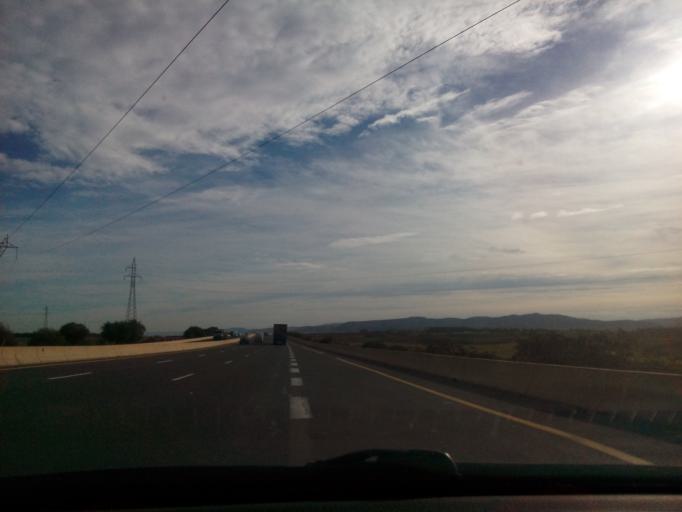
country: DZ
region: Mascara
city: Sig
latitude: 35.5430
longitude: -0.3747
